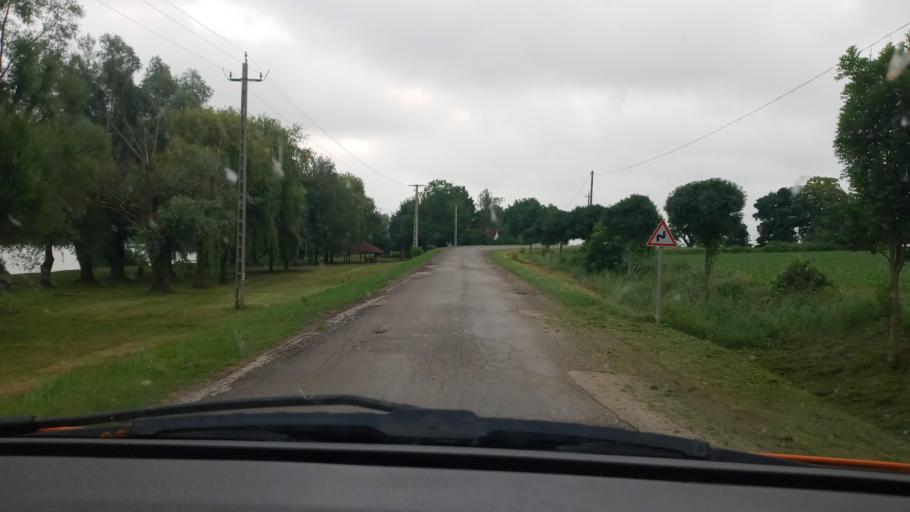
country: HU
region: Baranya
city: Szigetvar
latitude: 46.0767
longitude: 17.8604
